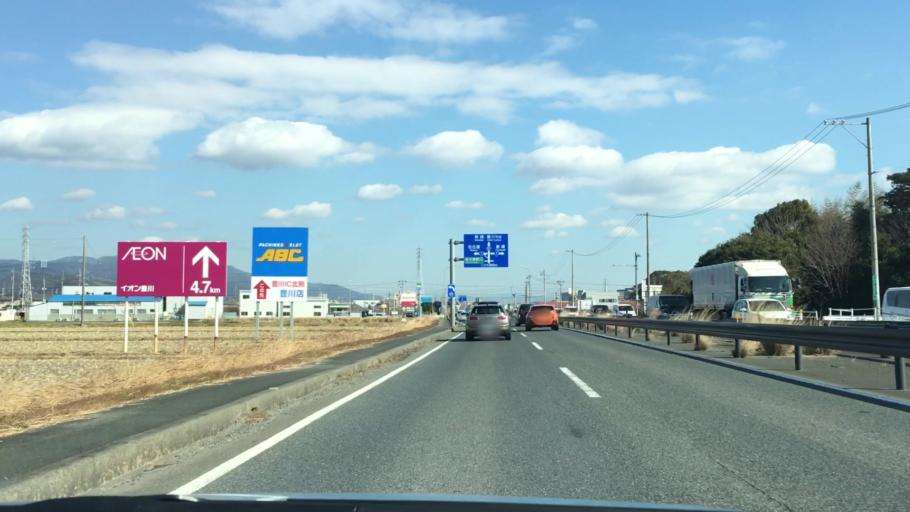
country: JP
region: Aichi
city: Kozakai-cho
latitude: 34.8221
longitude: 137.3317
